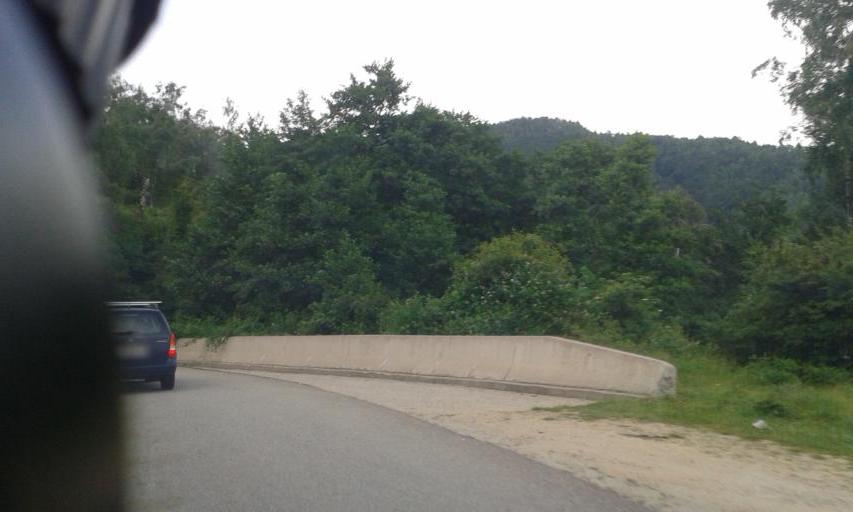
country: RO
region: Gorj
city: Novaci-Straini
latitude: 45.2069
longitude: 23.6940
